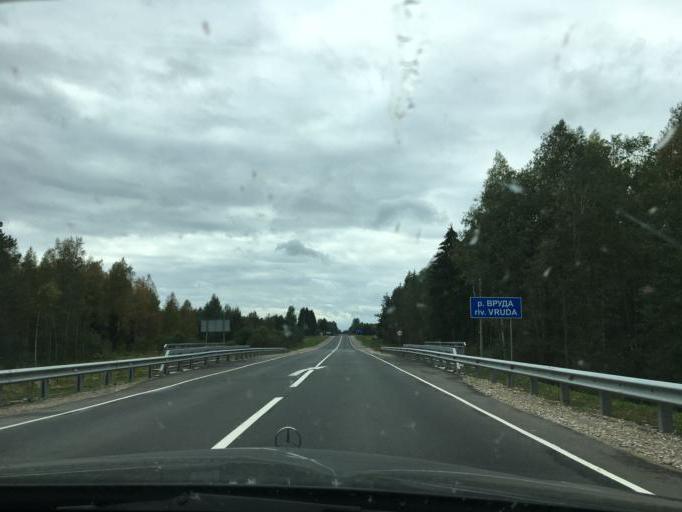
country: RU
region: Pskov
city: Pechory
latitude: 57.6596
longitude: 27.4686
